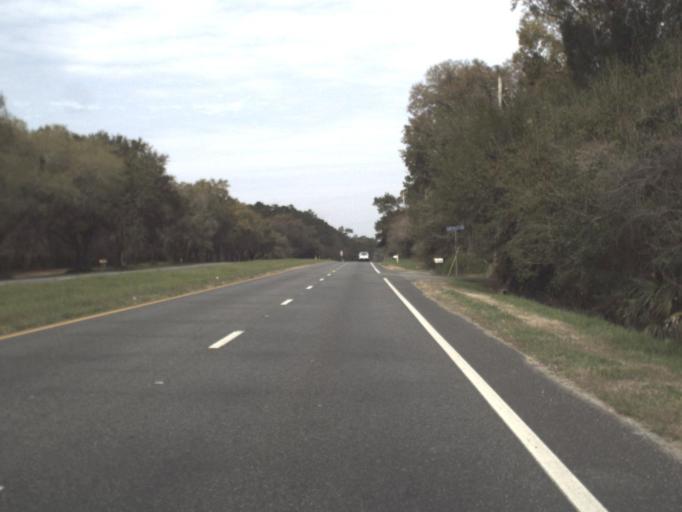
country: US
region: Florida
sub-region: Gadsden County
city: Midway
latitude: 30.4641
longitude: -84.3944
